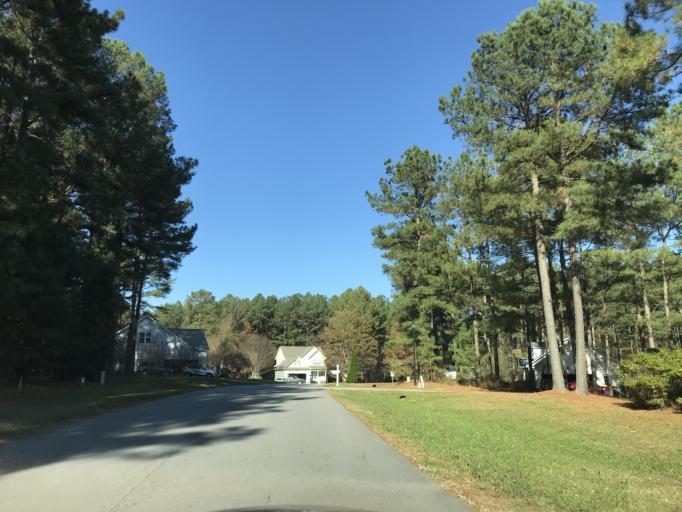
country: US
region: North Carolina
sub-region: Wake County
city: Rolesville
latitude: 35.9667
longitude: -78.3689
